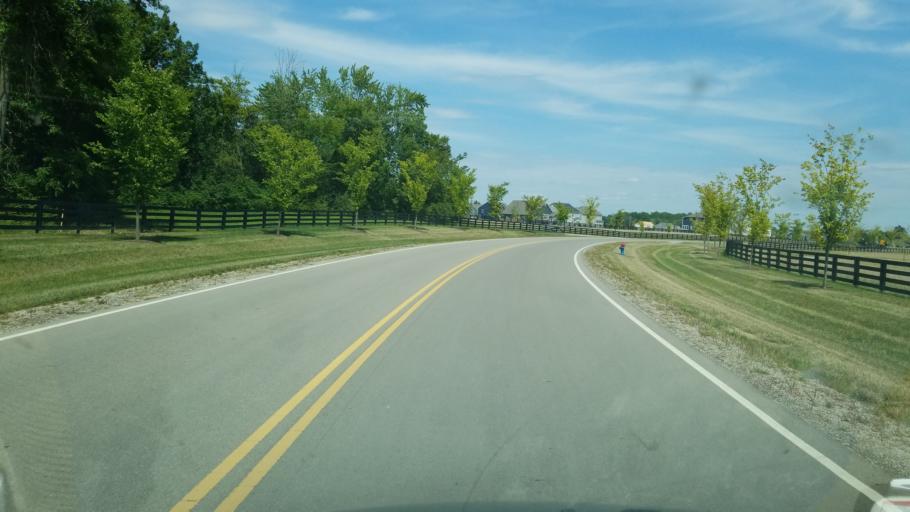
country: US
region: Ohio
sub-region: Union County
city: New California
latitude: 40.1859
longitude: -83.1858
